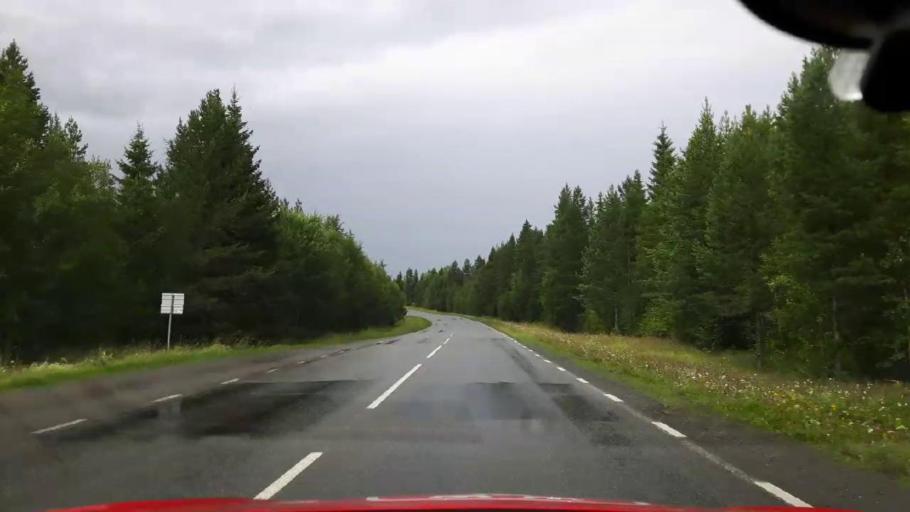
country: SE
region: Jaemtland
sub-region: Krokoms Kommun
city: Krokom
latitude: 63.3310
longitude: 14.2875
